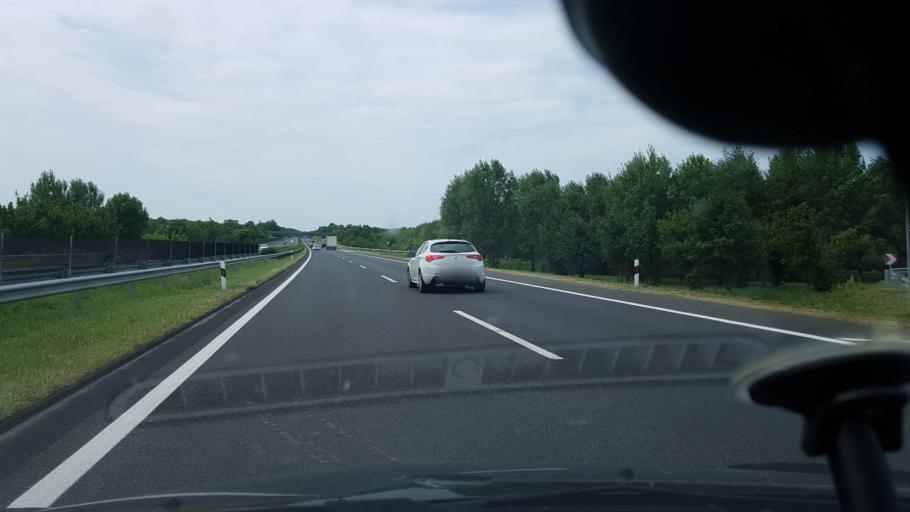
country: HU
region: Somogy
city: Balatonszarszo
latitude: 46.8028
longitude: 17.8125
